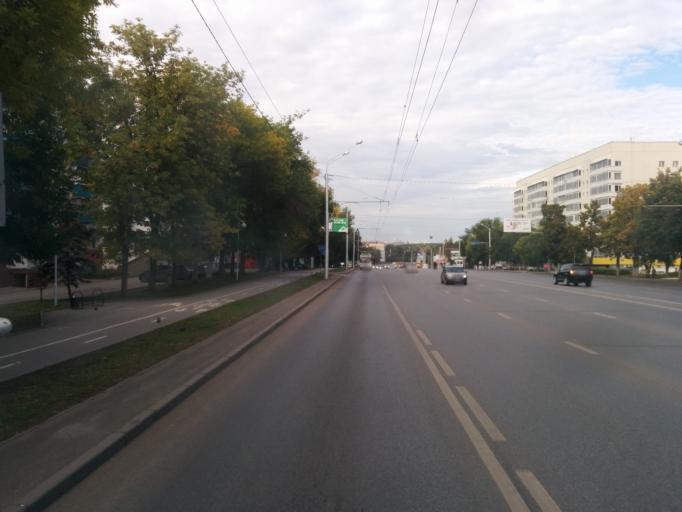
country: RU
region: Bashkortostan
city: Ufa
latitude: 54.7925
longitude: 56.0369
